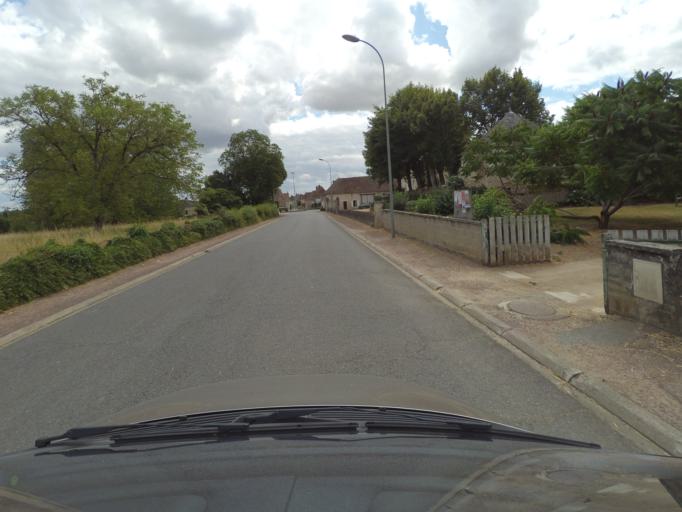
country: FR
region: Centre
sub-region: Departement de l'Indre
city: Belabre
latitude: 46.4691
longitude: 1.0381
